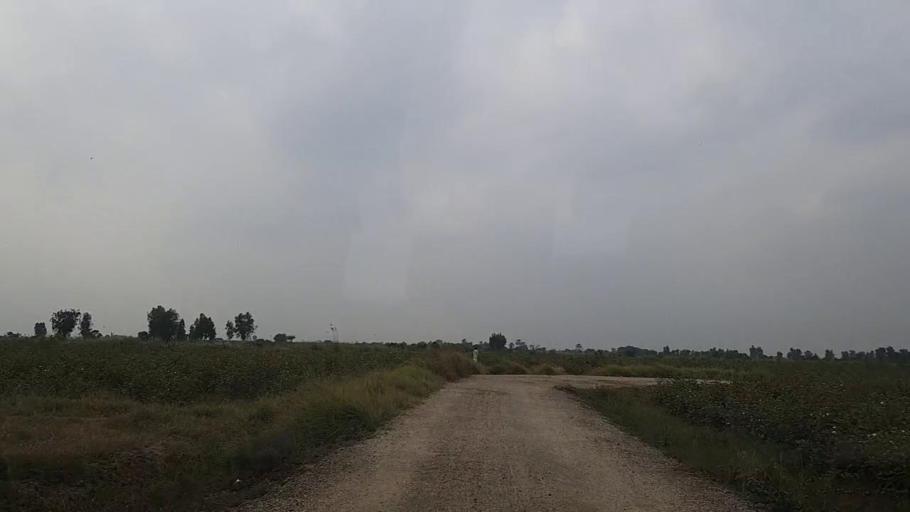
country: PK
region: Sindh
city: Mirpur Sakro
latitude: 24.6191
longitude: 67.7180
